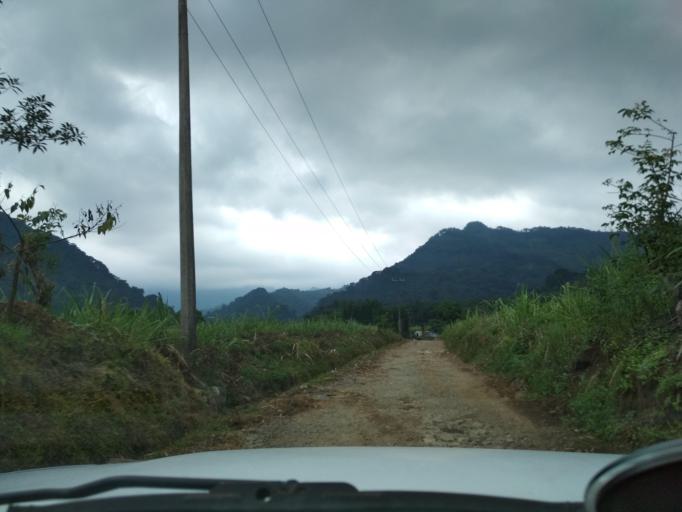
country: MX
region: Veracruz
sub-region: Fortin
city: Santa Lucia Potrerillo
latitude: 18.9497
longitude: -97.0607
